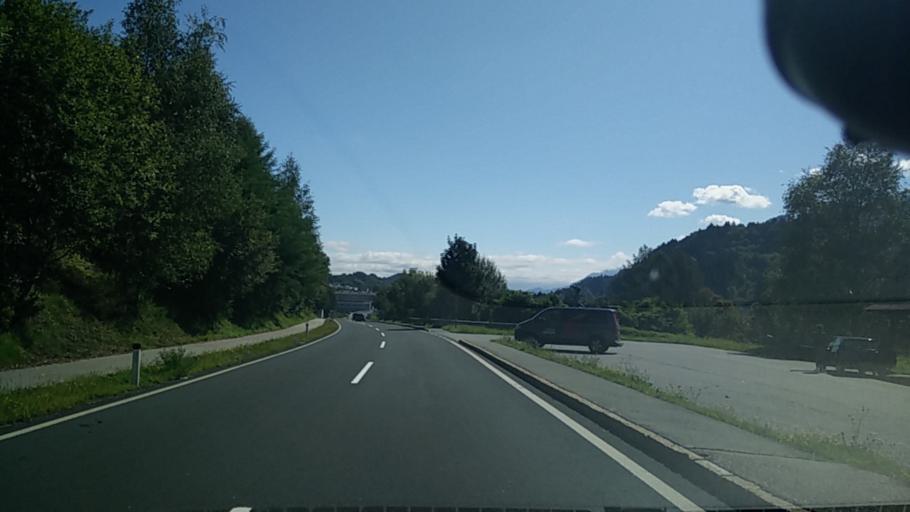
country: AT
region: Carinthia
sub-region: Politischer Bezirk Villach Land
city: Hohenthurn
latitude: 46.5496
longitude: 13.6868
